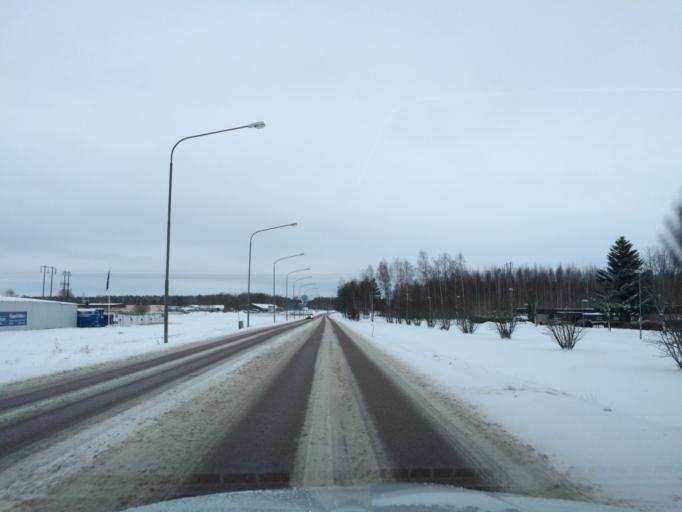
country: SE
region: Vaestmanland
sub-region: Hallstahammars Kommun
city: Hallstahammar
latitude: 59.6080
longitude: 16.2463
